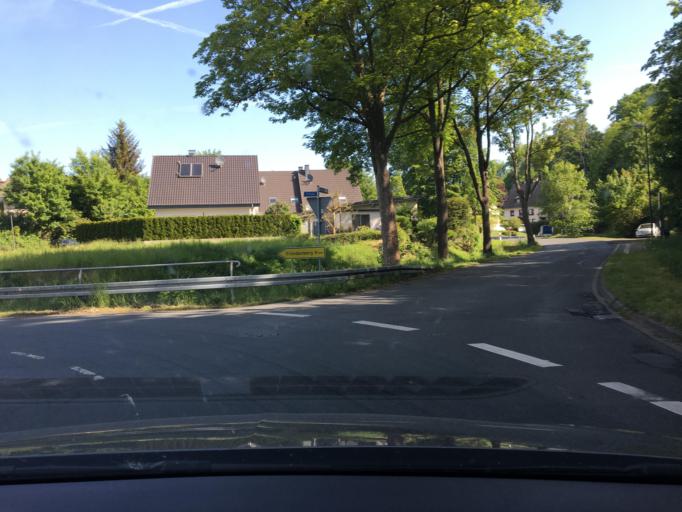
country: DE
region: North Rhine-Westphalia
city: Wickede
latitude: 51.4985
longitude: 7.8507
